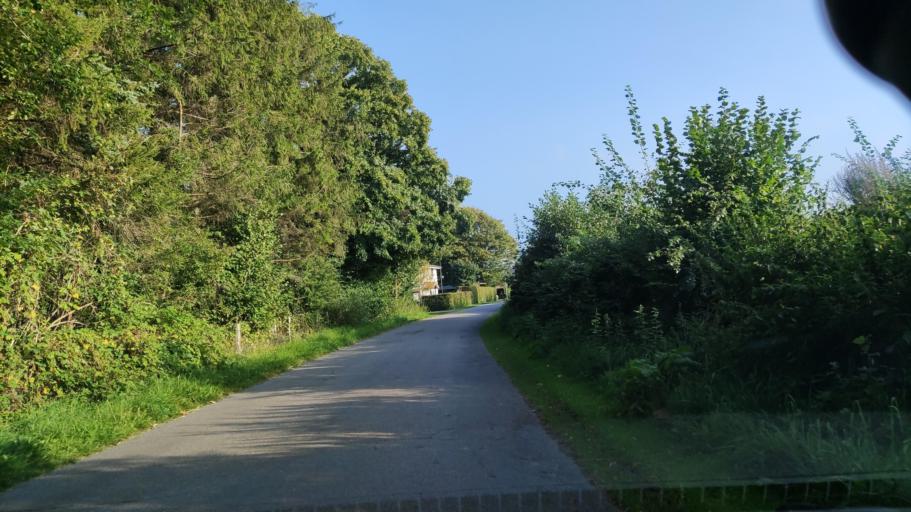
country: DE
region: Schleswig-Holstein
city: Struvenhutten
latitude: 53.8611
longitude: 10.0694
